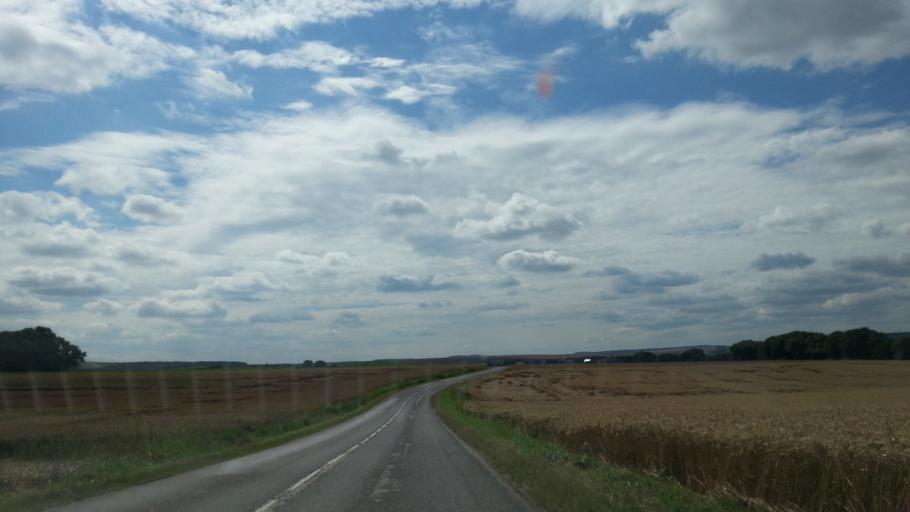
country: FR
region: Lorraine
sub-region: Departement de la Meuse
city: Thierville-sur-Meuse
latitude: 49.2103
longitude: 5.3288
